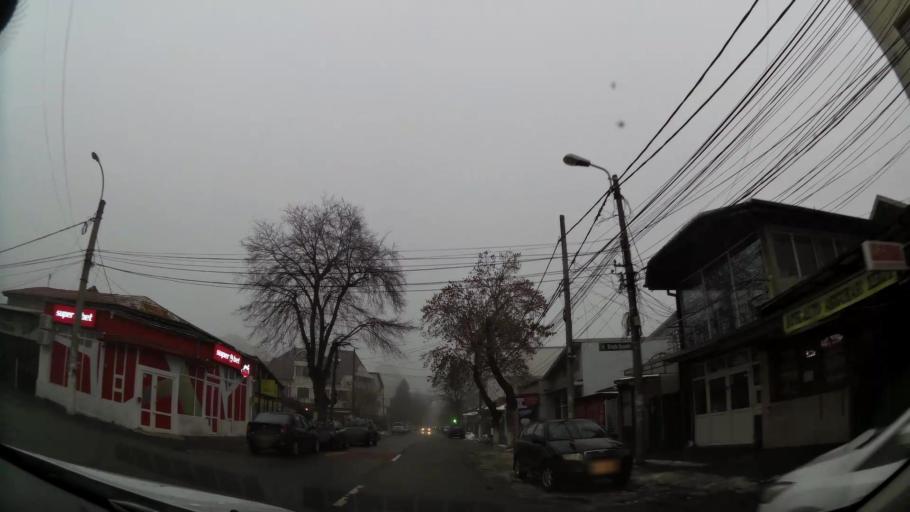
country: RO
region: Ilfov
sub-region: Comuna Chiajna
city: Rosu
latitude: 44.4849
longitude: 26.0345
